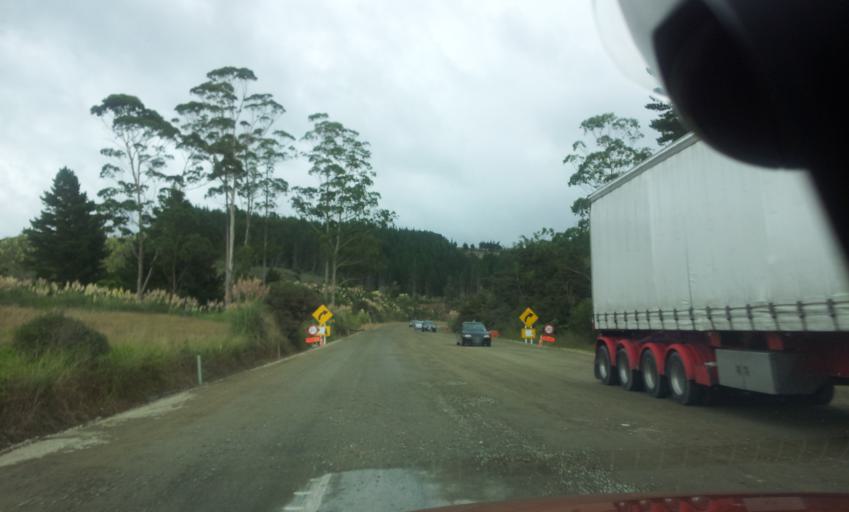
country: NZ
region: Auckland
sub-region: Auckland
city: Wellsford
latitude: -36.2127
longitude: 174.4679
